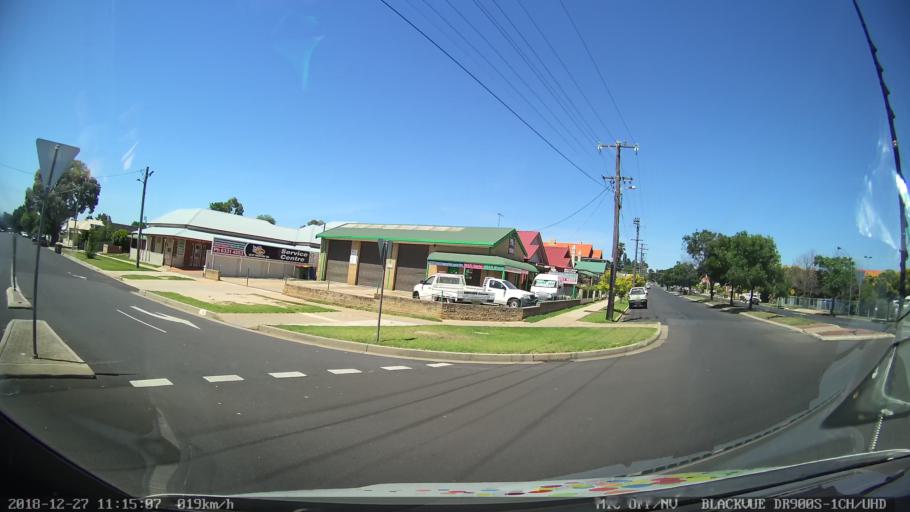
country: AU
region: New South Wales
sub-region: Bathurst Regional
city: Bathurst
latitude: -33.4215
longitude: 149.5755
